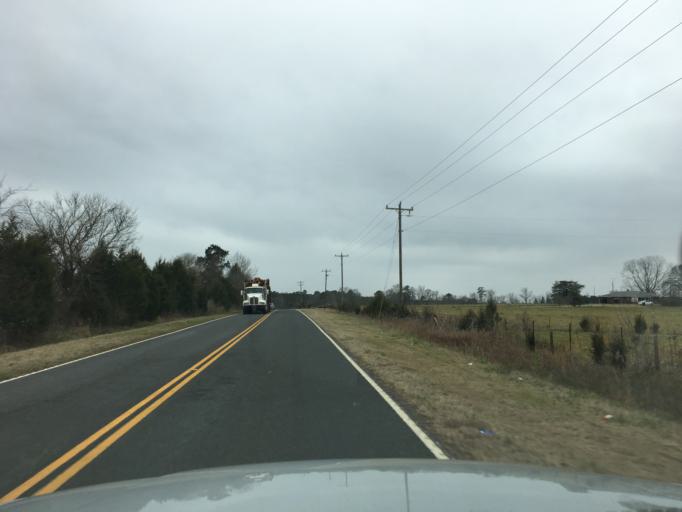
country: US
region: South Carolina
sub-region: Greenwood County
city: Greenwood
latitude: 34.1165
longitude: -82.1758
